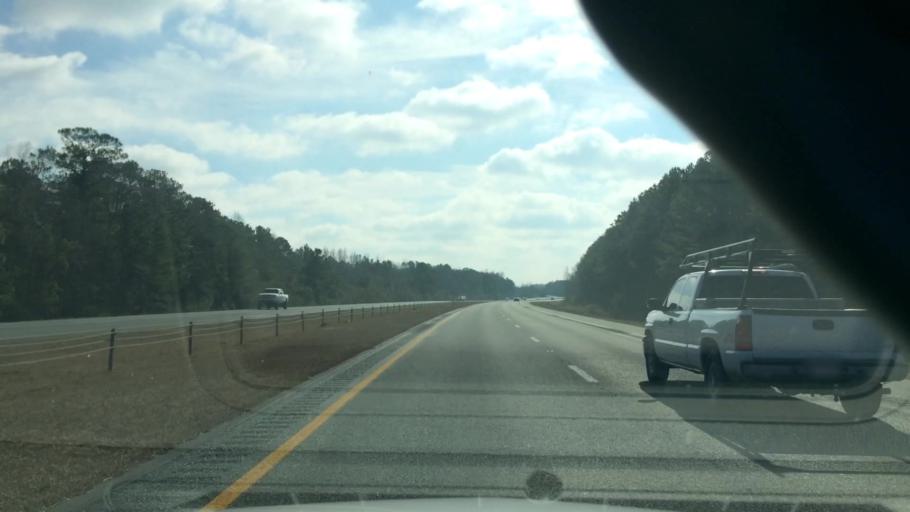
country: US
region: North Carolina
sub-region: Duplin County
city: Wallace
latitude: 34.6979
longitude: -77.9448
